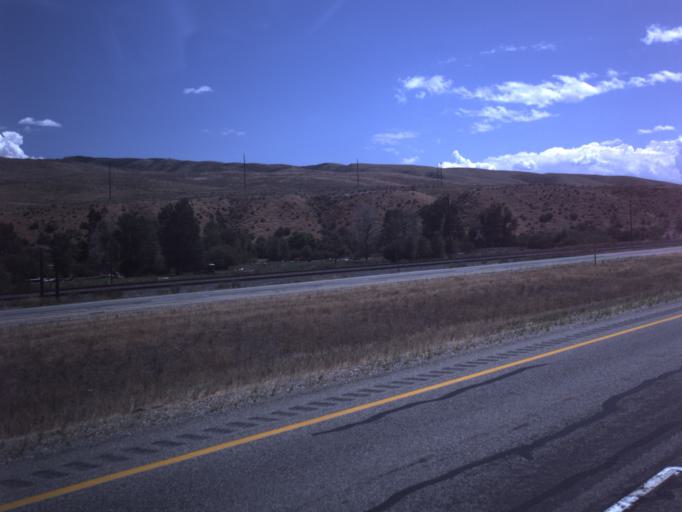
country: US
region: Utah
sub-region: Summit County
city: Coalville
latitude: 41.0236
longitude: -111.4961
